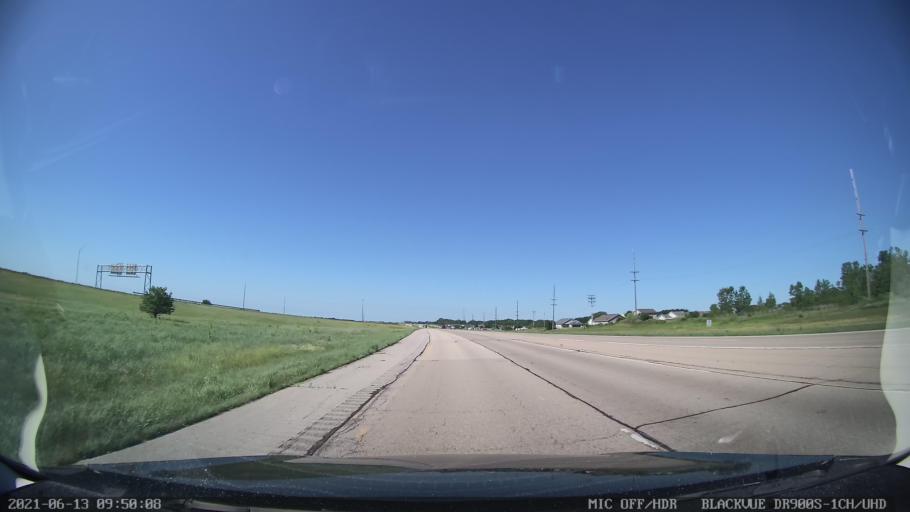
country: US
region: Illinois
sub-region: McLean County
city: Bloomington
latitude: 40.4372
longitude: -89.0271
